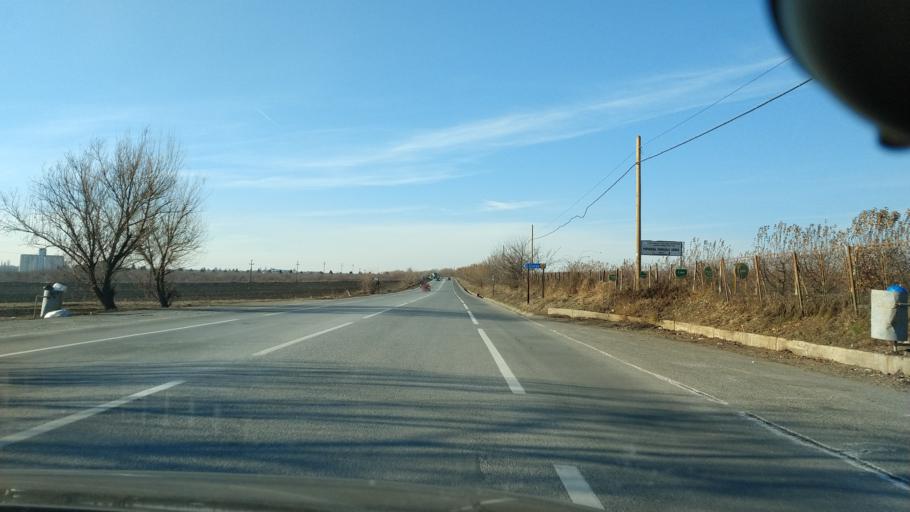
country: RO
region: Iasi
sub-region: Comuna Baltati
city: Baltati
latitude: 47.2227
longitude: 27.1698
